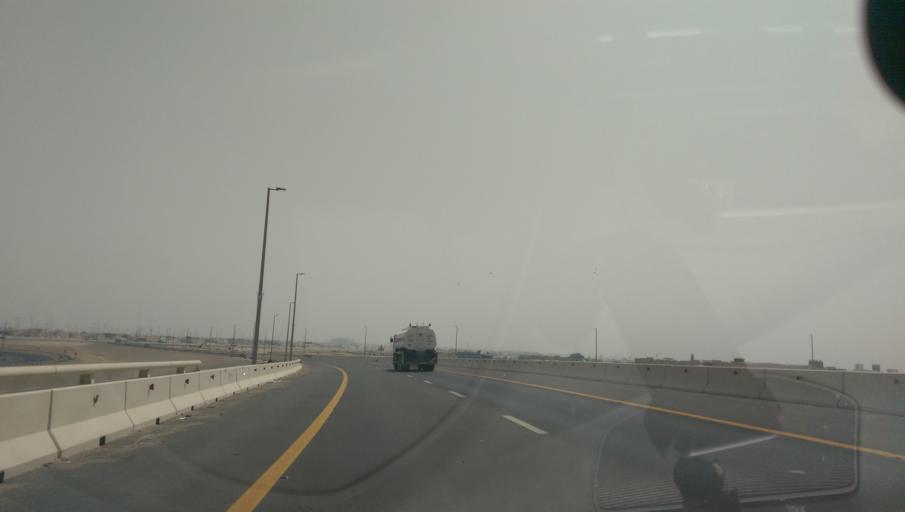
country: AE
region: Abu Dhabi
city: Abu Dhabi
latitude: 24.2846
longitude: 54.5569
